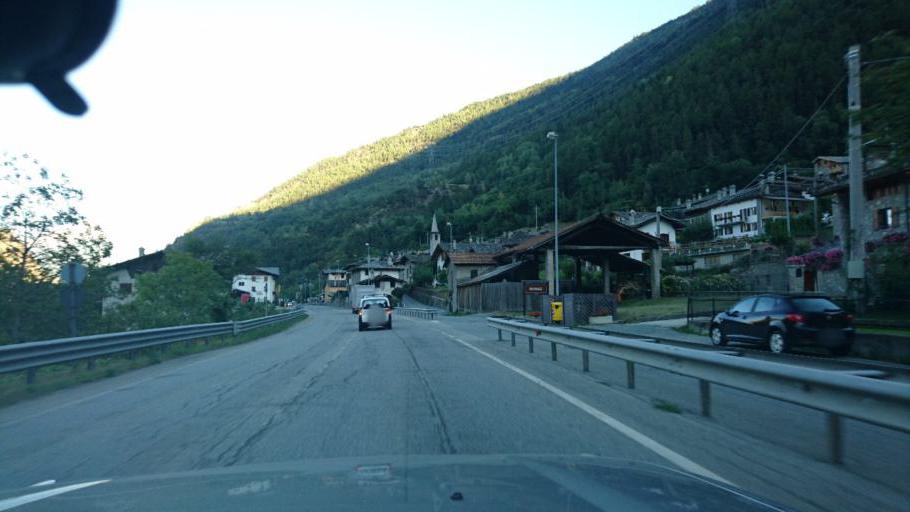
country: IT
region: Aosta Valley
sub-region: Valle d'Aosta
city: Avise
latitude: 45.7072
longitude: 7.1248
